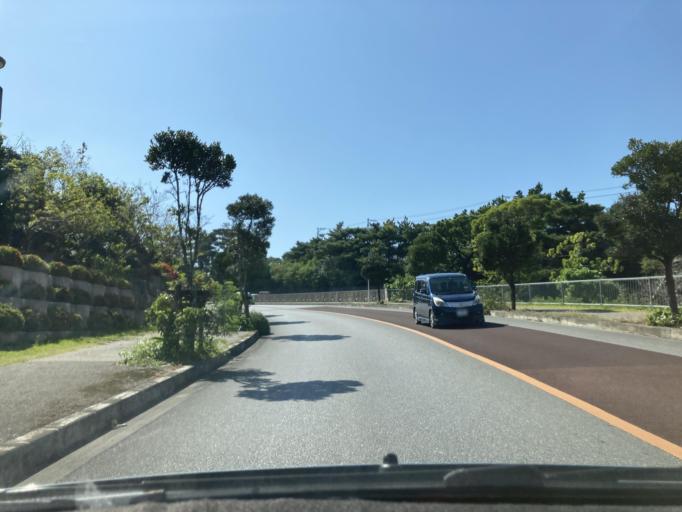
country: JP
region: Okinawa
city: Ginowan
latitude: 26.2430
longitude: 127.7256
